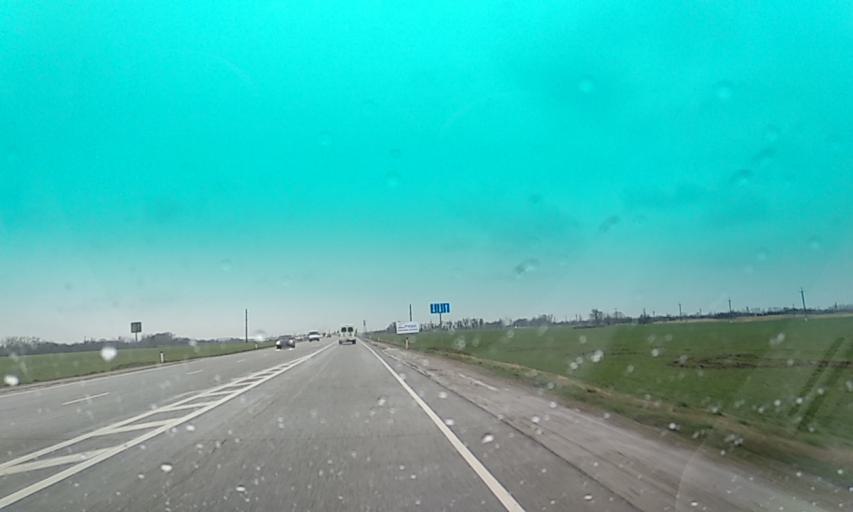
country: RU
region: Krasnodarskiy
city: Belorechensk
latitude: 44.8206
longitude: 39.8493
